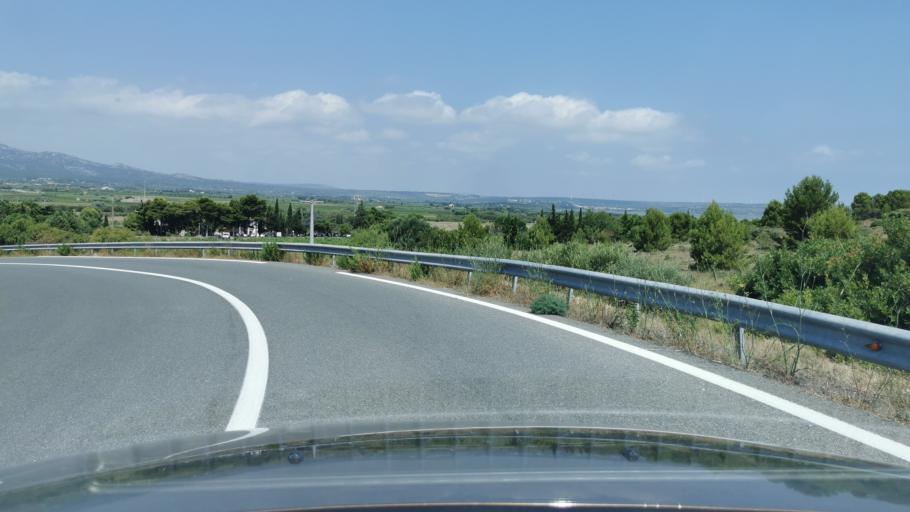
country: FR
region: Languedoc-Roussillon
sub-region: Departement de l'Aude
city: Leucate
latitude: 42.9309
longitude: 3.0156
